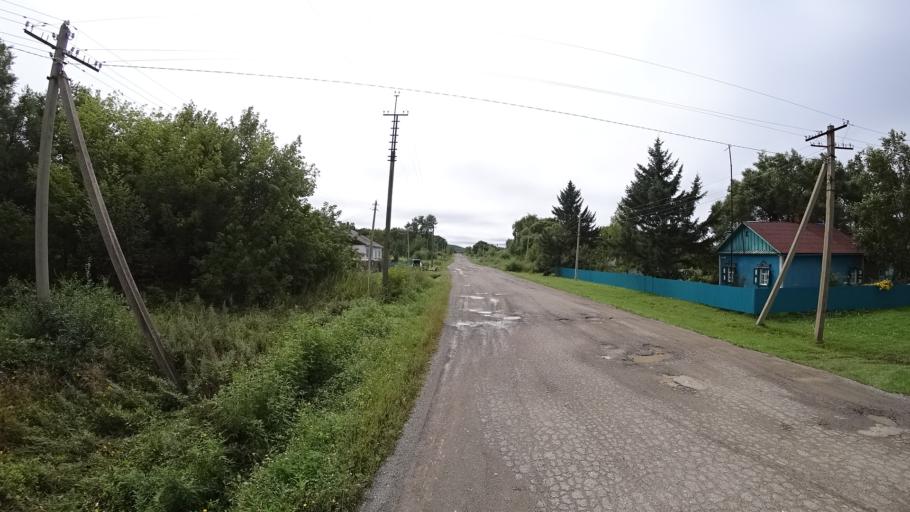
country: RU
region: Primorskiy
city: Lyalichi
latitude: 44.0760
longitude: 132.4716
